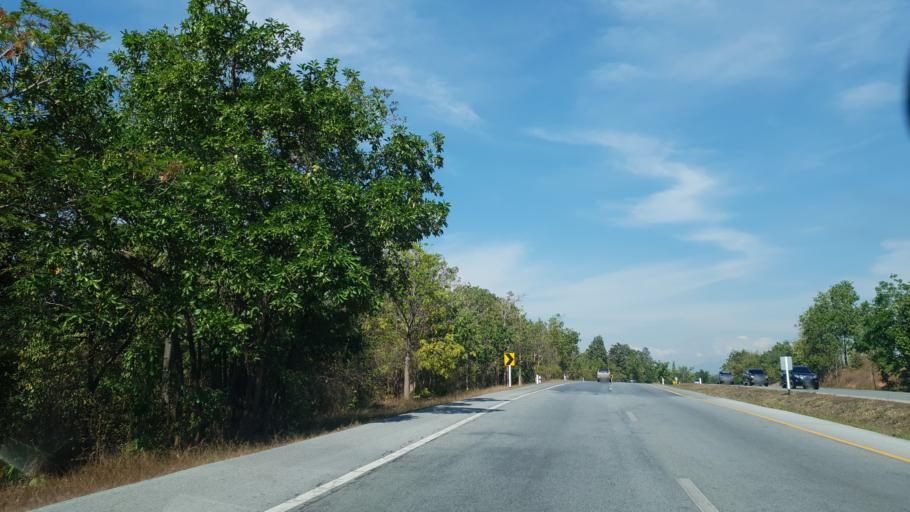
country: TH
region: Uttaradit
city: Thong Saen Khan
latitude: 17.4224
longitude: 100.2259
